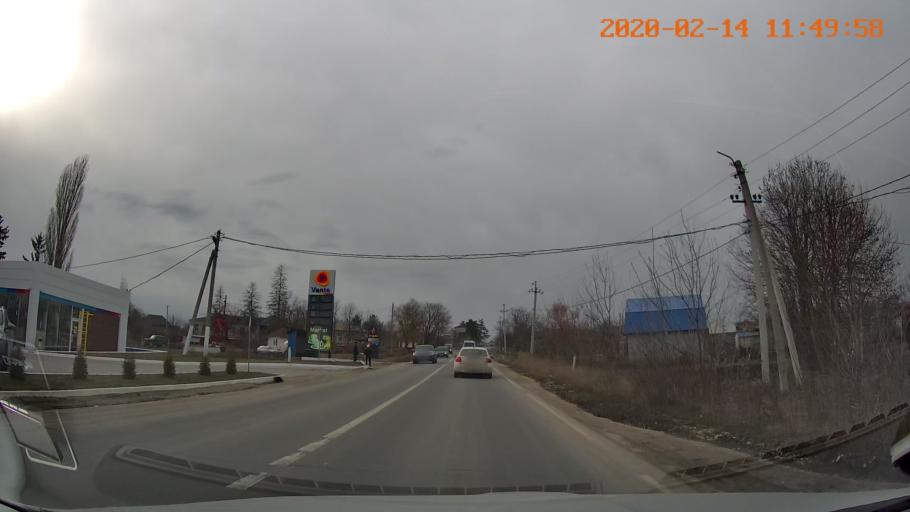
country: RO
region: Botosani
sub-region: Comuna Radauti-Prut
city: Miorcani
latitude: 48.2972
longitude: 26.9357
